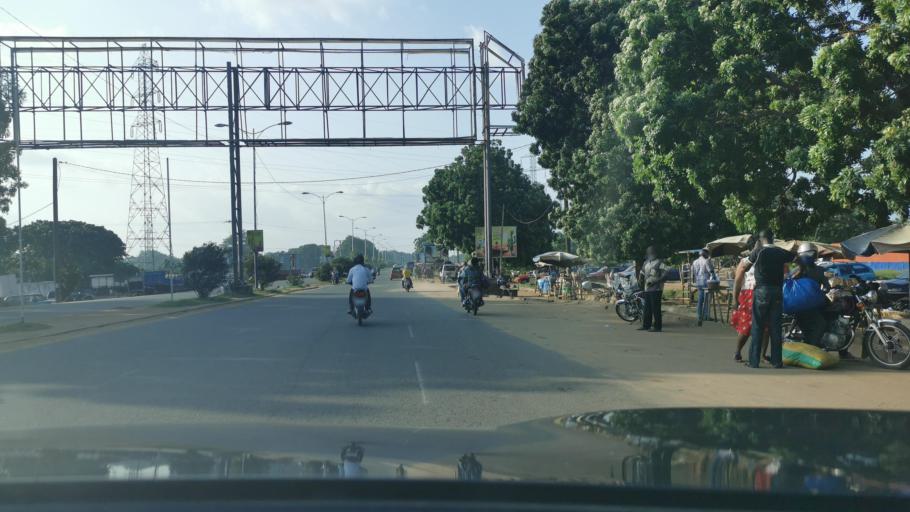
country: TG
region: Maritime
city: Lome
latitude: 6.1956
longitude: 1.2090
